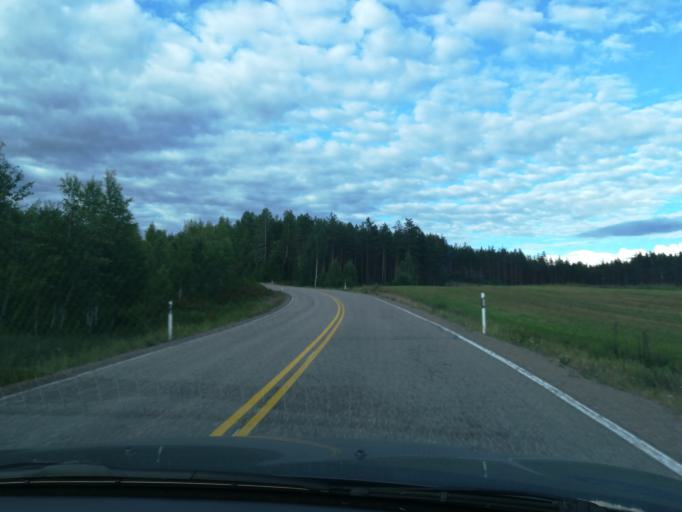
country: FI
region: Southern Savonia
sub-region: Mikkeli
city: Puumala
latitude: 61.5010
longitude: 27.8607
